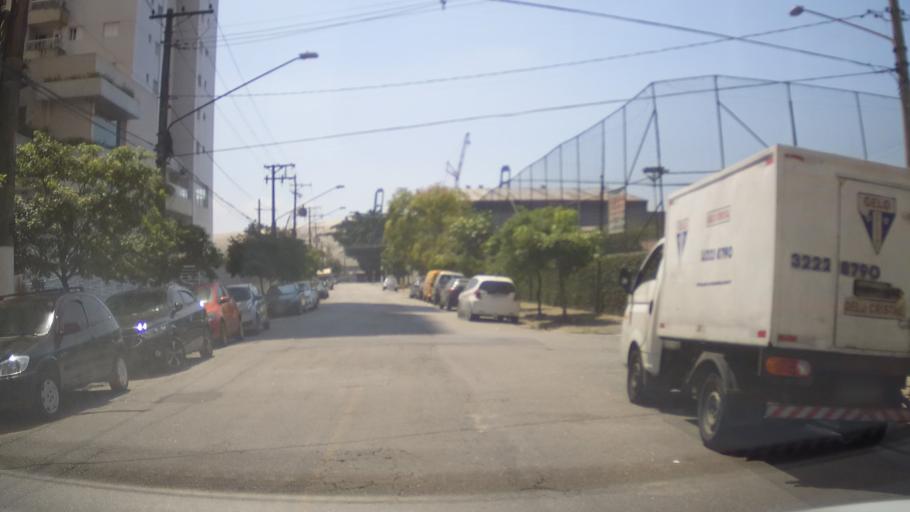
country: BR
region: Sao Paulo
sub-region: Guaruja
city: Guaruja
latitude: -23.9820
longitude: -46.2962
